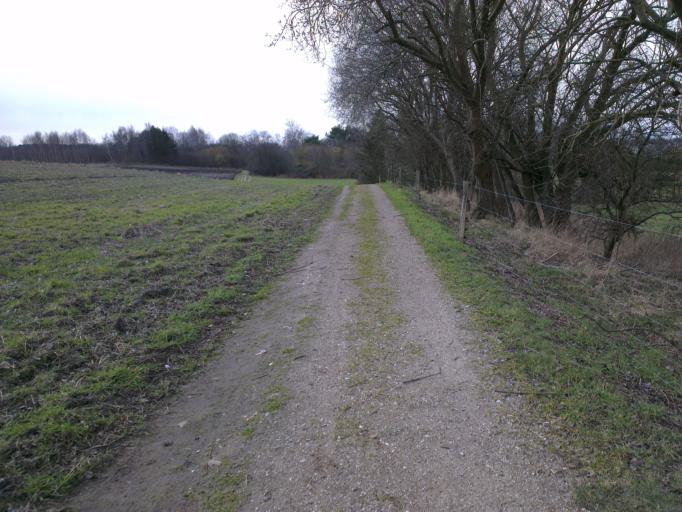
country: DK
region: Zealand
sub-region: Lejre Kommune
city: Ejby
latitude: 55.7751
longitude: 11.8615
